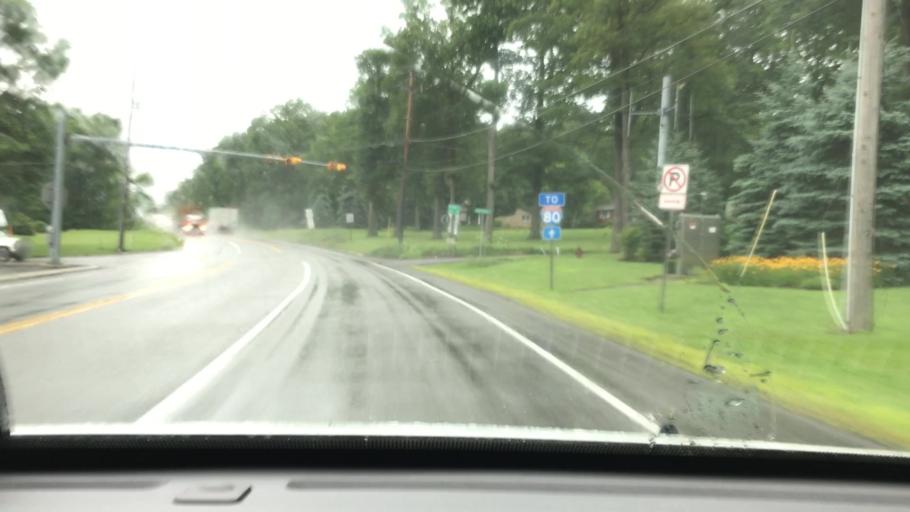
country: US
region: Pennsylvania
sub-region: Clearfield County
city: Osceola Mills
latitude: 40.8079
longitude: -78.2251
